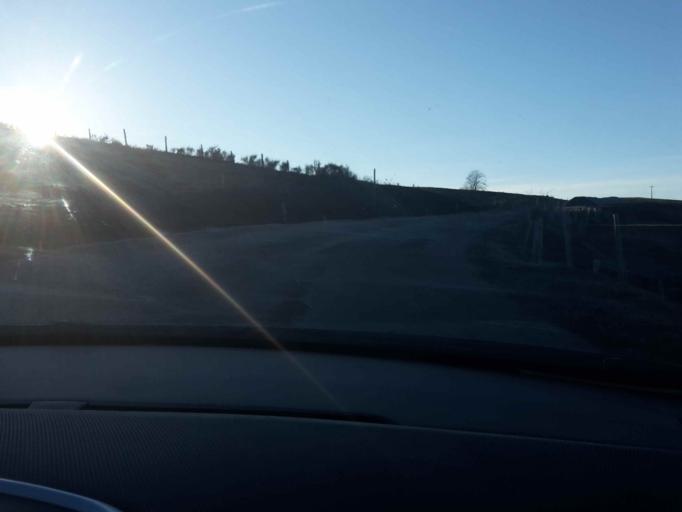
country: FR
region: Auvergne
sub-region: Departement du Cantal
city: Riom-es-Montagnes
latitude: 45.2642
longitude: 2.5652
